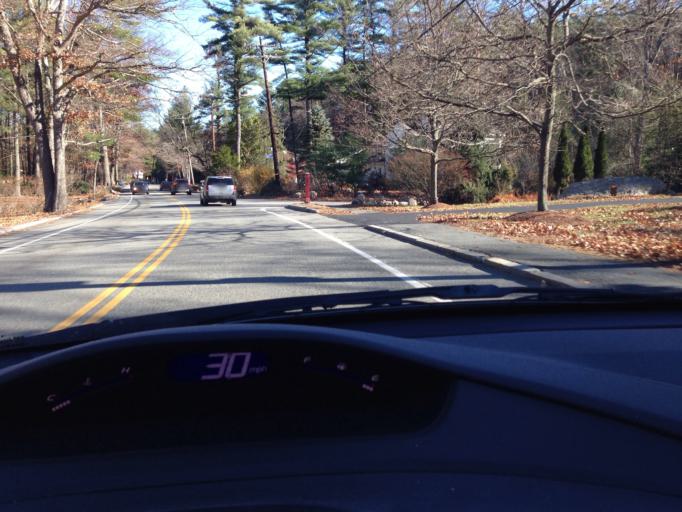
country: US
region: Massachusetts
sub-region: Middlesex County
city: Bedford
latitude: 42.4981
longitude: -71.2559
